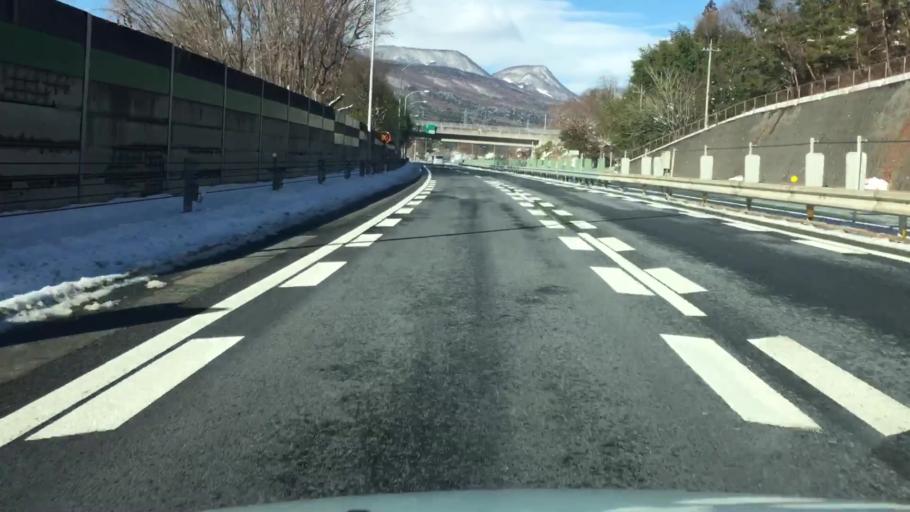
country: JP
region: Gunma
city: Numata
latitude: 36.6988
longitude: 138.9897
